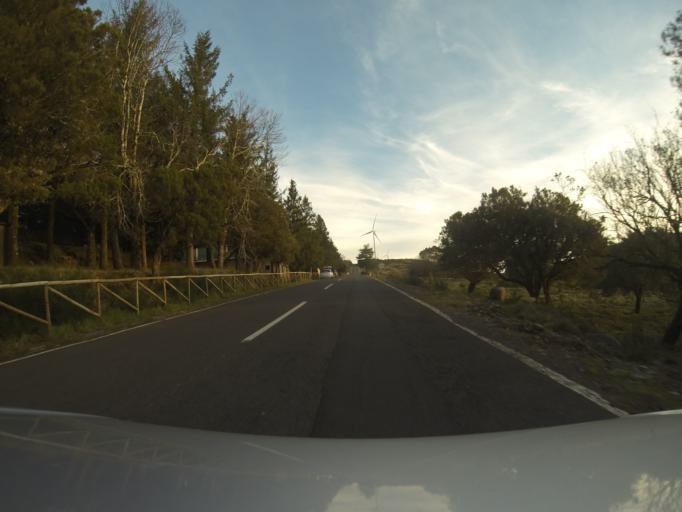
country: PT
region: Madeira
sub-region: Sao Vicente
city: Sao Vicente
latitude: 32.7534
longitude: -17.0587
